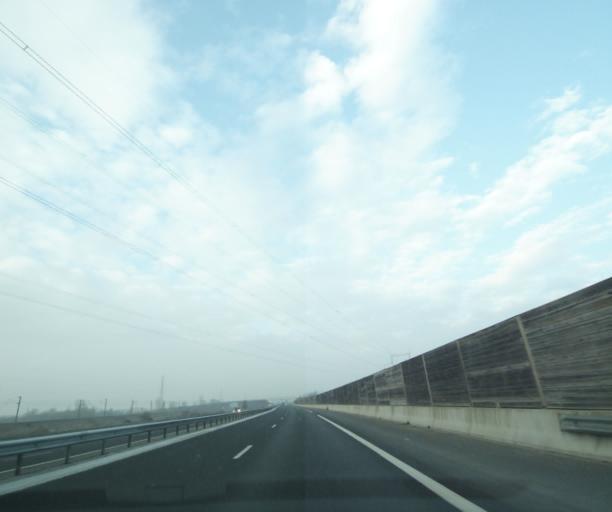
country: FR
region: Rhone-Alpes
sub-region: Departement de l'Ain
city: Tramoyes
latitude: 45.8602
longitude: 4.9665
